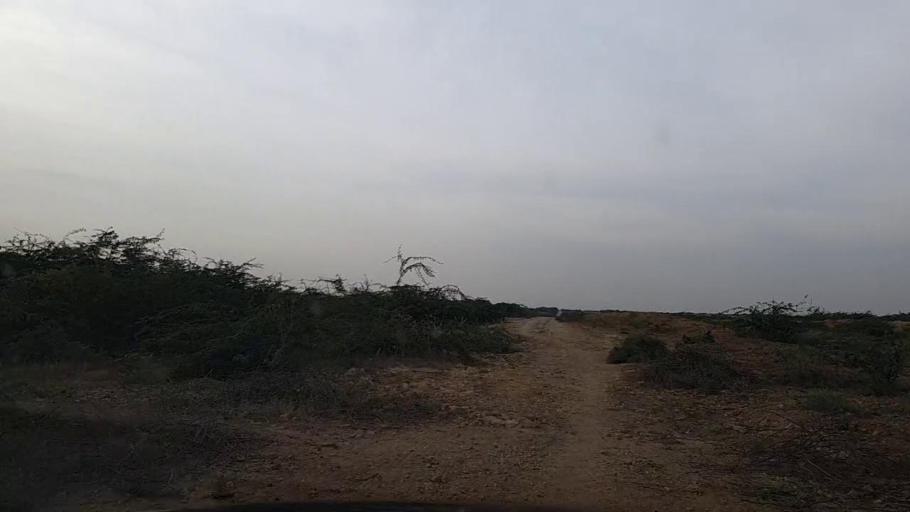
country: PK
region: Sindh
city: Gharo
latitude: 24.7893
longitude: 67.5525
